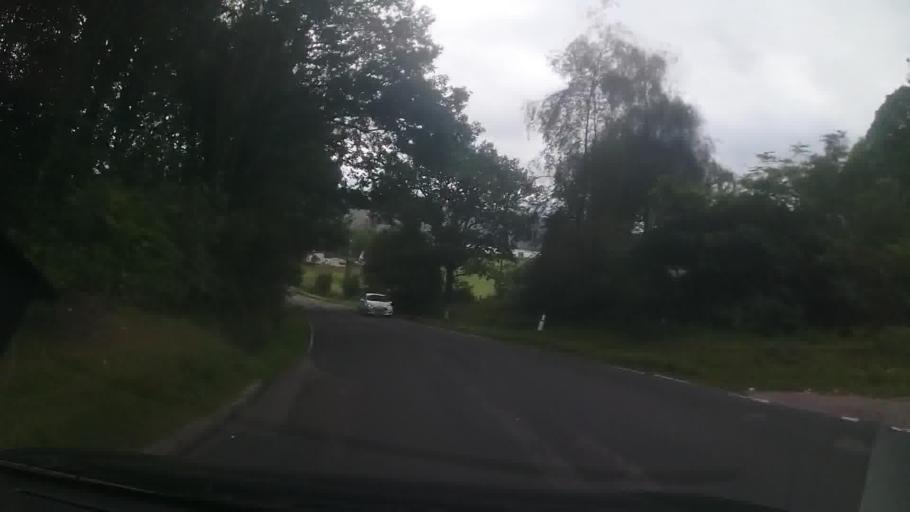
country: GB
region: Scotland
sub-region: Argyll and Bute
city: Garelochhead
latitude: 56.2336
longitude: -5.0806
